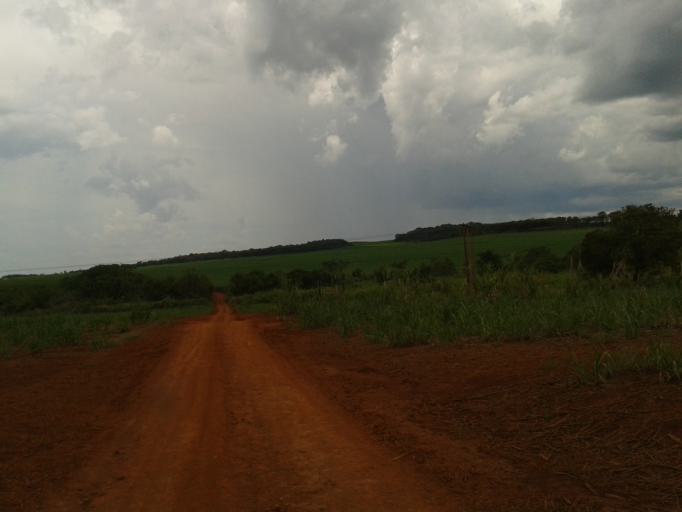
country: BR
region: Minas Gerais
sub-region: Centralina
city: Centralina
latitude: -18.6660
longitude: -49.2322
